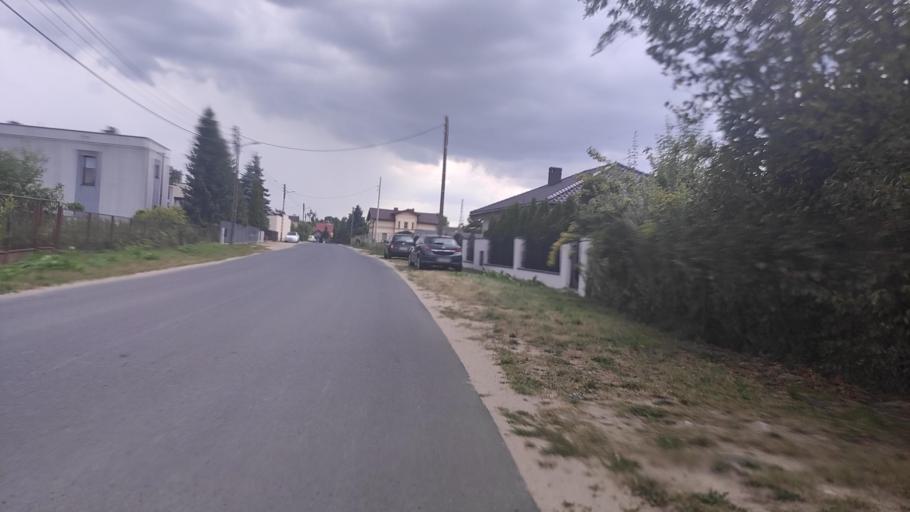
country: PL
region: Greater Poland Voivodeship
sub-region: Powiat poznanski
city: Swarzedz
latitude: 52.3887
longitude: 17.1173
